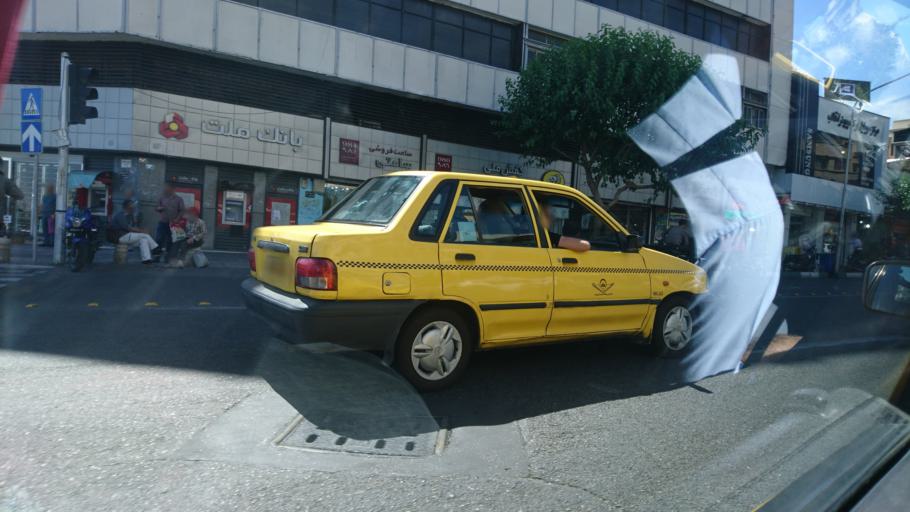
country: IR
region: Tehran
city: Tehran
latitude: 35.7010
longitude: 51.3930
